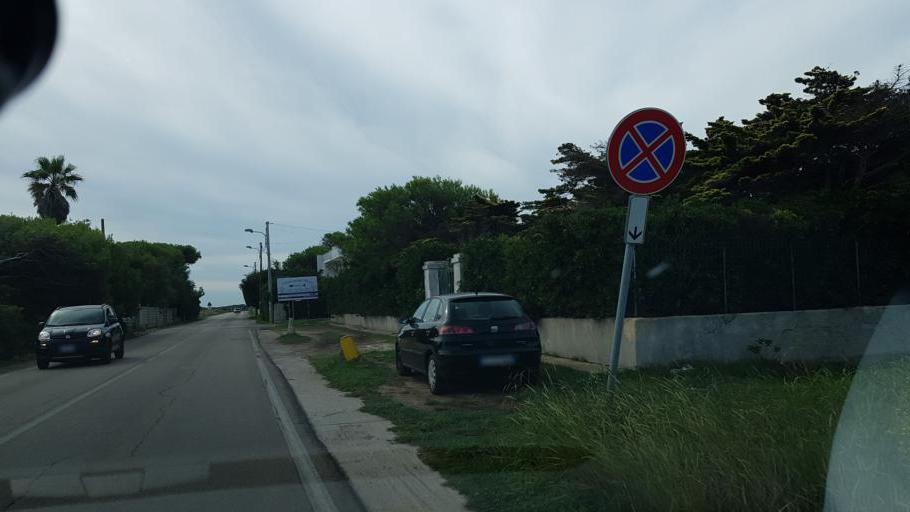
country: IT
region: Apulia
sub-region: Provincia di Lecce
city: Borgagne
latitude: 40.2827
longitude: 18.4311
